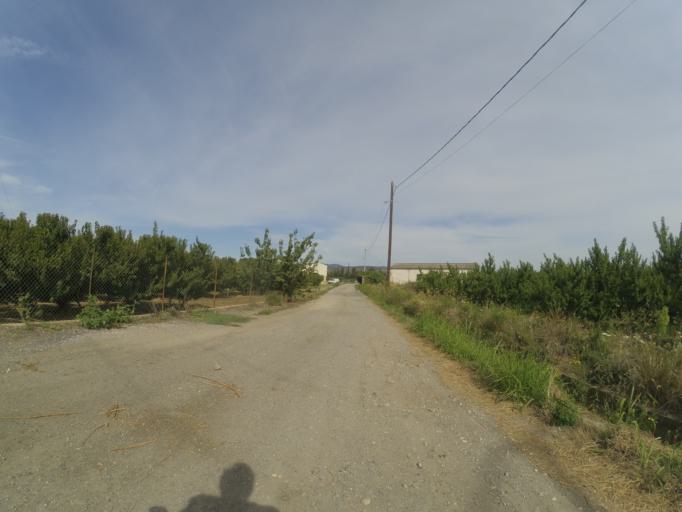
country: FR
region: Languedoc-Roussillon
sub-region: Departement des Pyrenees-Orientales
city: Ille-sur-Tet
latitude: 42.6565
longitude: 2.6339
